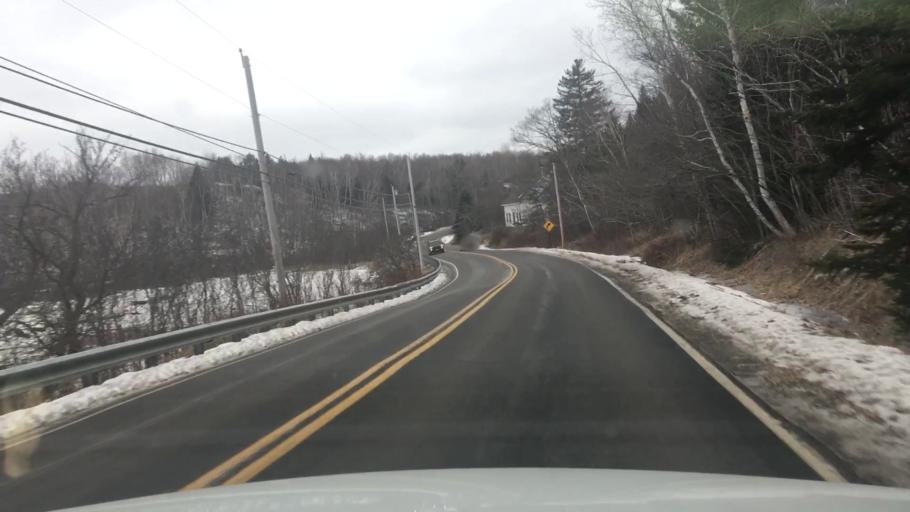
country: US
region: Maine
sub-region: Washington County
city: East Machias
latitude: 44.7242
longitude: -67.3842
